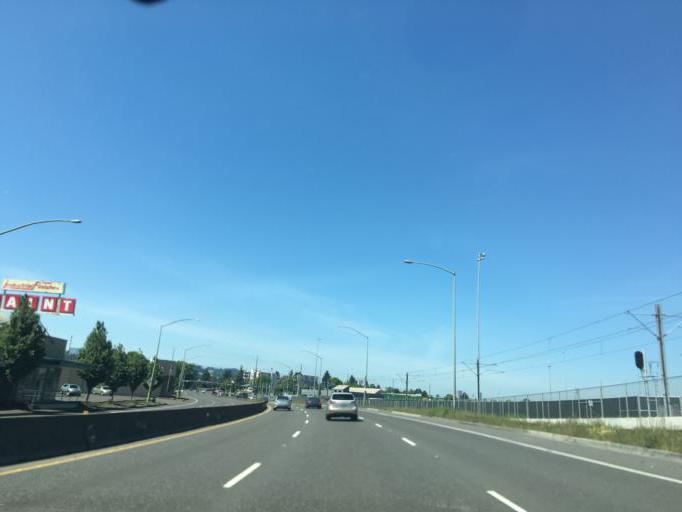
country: US
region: Oregon
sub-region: Clackamas County
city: Milwaukie
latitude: 45.4840
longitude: -122.6441
